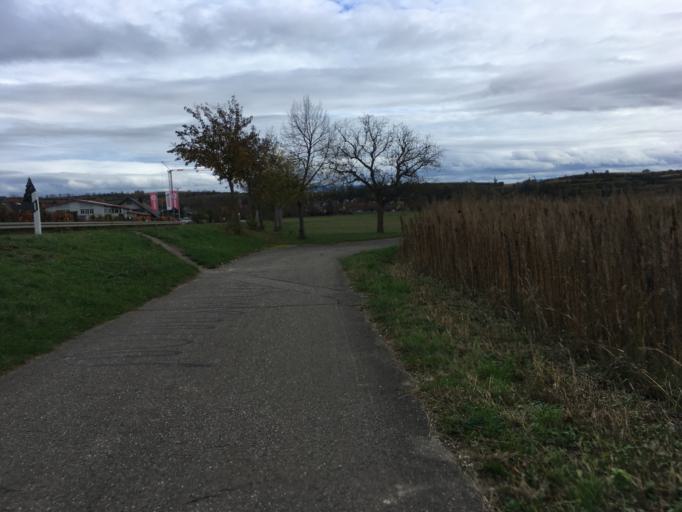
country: DE
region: Baden-Wuerttemberg
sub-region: Freiburg Region
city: Merdingen
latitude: 48.0217
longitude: 7.6765
